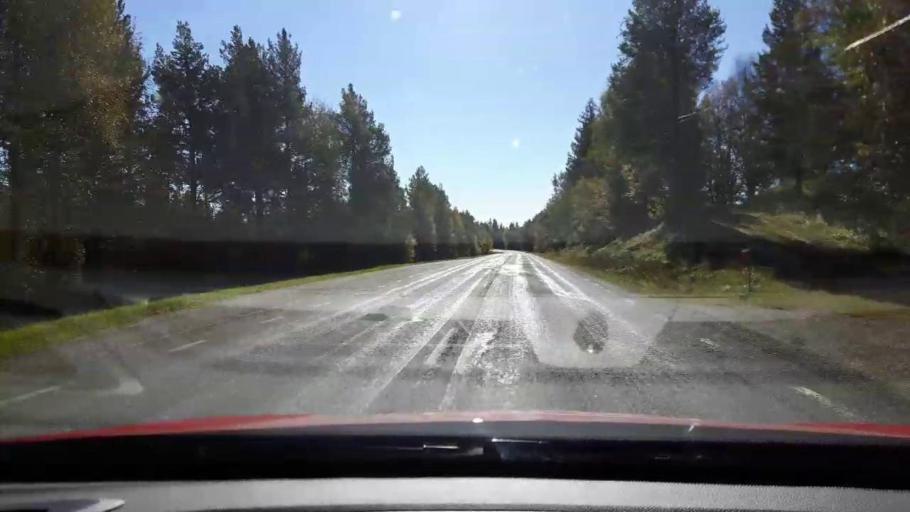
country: SE
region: Jaemtland
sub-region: Harjedalens Kommun
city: Sveg
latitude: 62.3426
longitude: 14.0376
